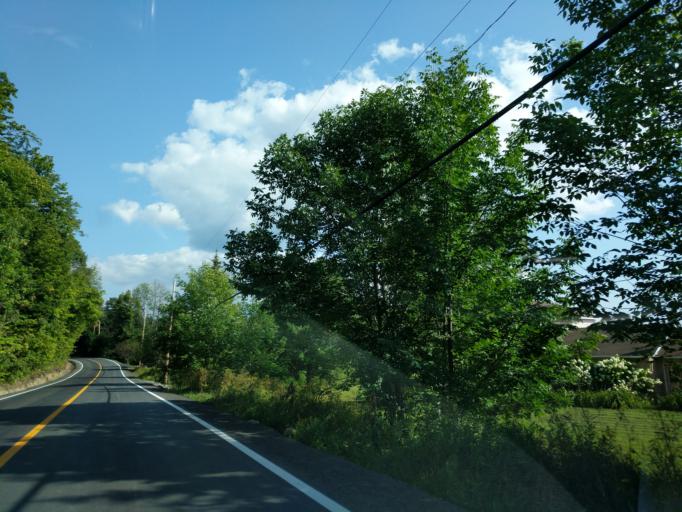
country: CA
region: Quebec
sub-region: Outaouais
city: Gatineau
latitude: 45.4868
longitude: -75.8758
